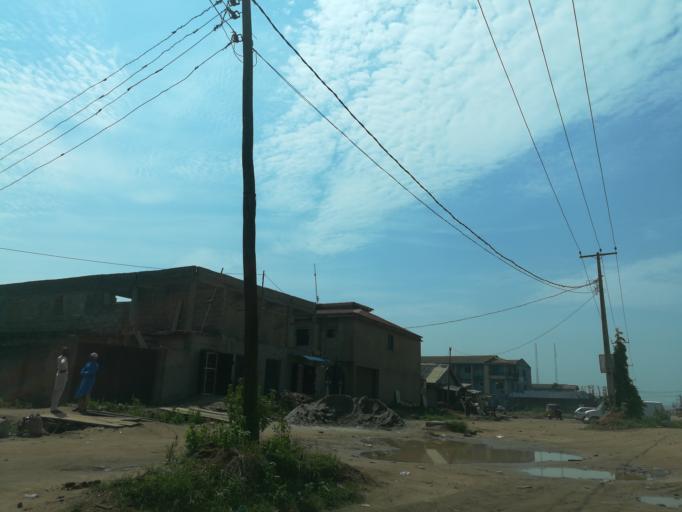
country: NG
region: Lagos
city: Ikorodu
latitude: 6.6431
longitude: 3.4803
